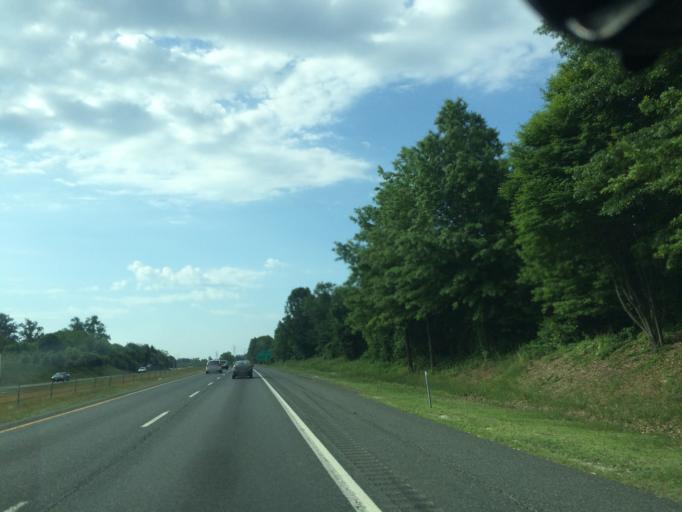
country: US
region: Maryland
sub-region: Baltimore County
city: Reisterstown
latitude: 39.4495
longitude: -76.8297
